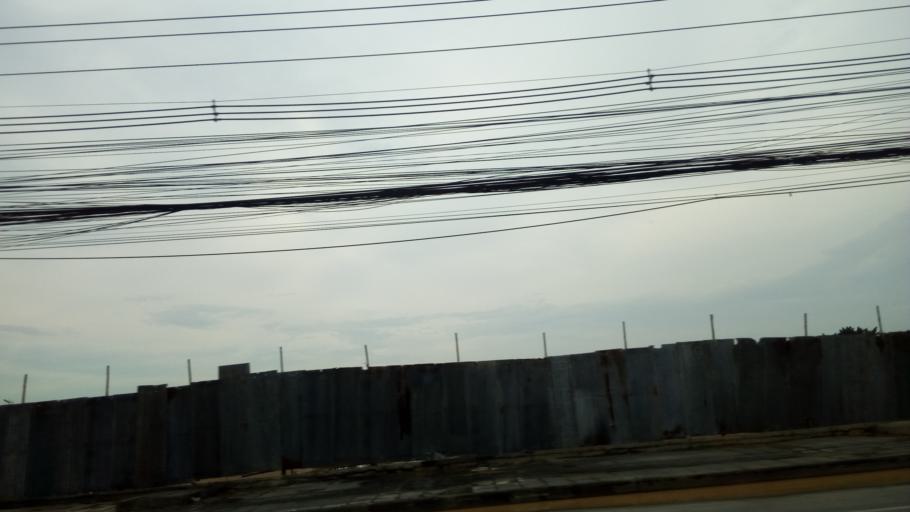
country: TH
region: Pathum Thani
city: Khlong Luang
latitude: 14.0652
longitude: 100.6246
